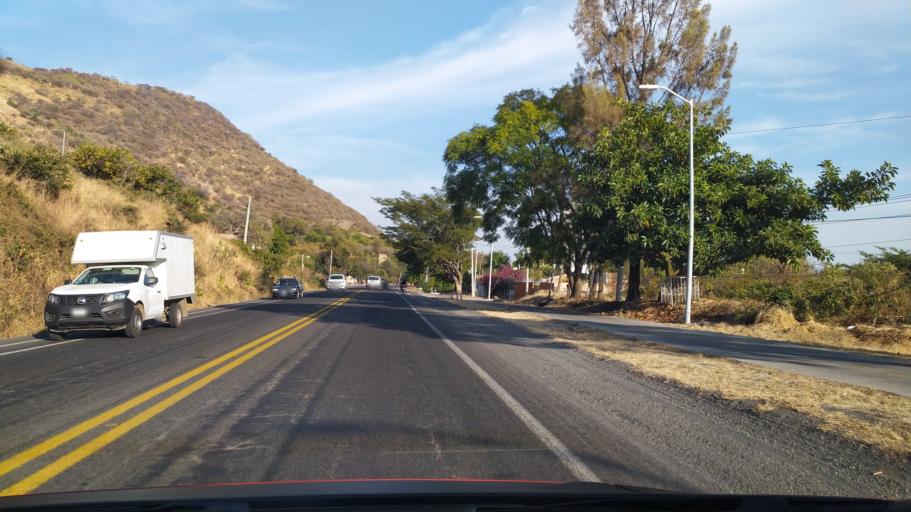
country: MX
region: Jalisco
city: Jamay
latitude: 20.2940
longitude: -102.7499
